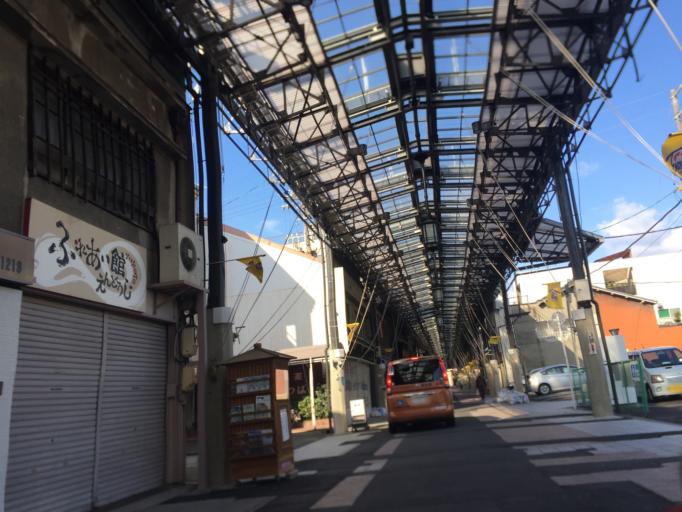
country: JP
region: Aichi
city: Nagoya-shi
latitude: 35.1761
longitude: 136.8925
